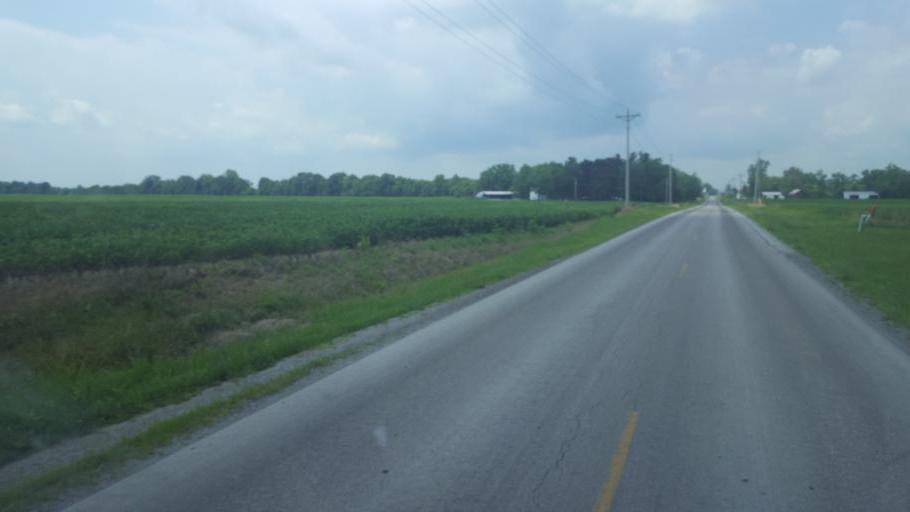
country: US
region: Ohio
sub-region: Hardin County
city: Kenton
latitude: 40.5855
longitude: -83.4907
